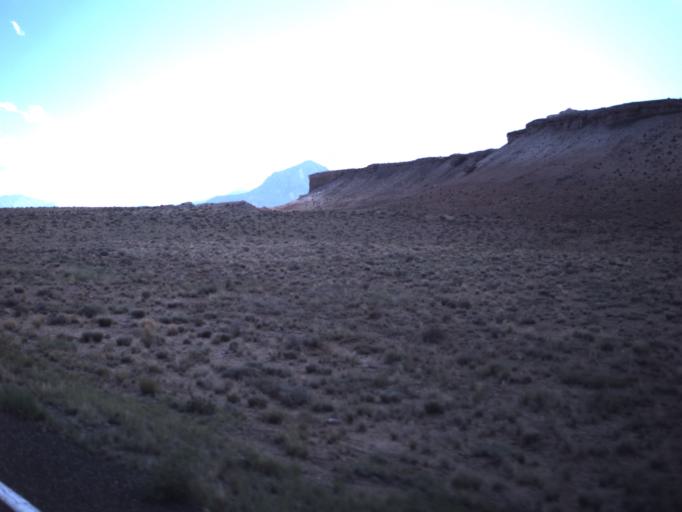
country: US
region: Utah
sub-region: Emery County
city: Ferron
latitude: 38.2814
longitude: -110.6627
